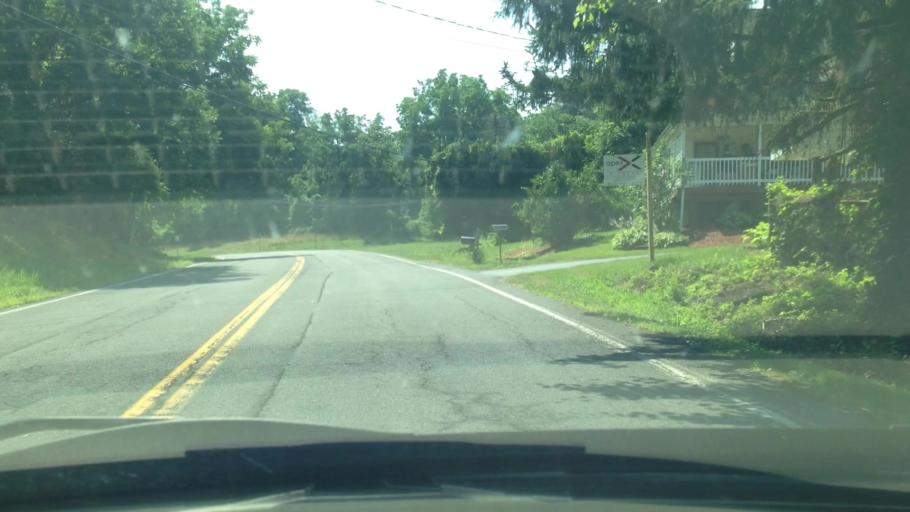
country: US
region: New York
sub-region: Ulster County
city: Port Ewen
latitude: 41.9004
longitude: -74.0012
